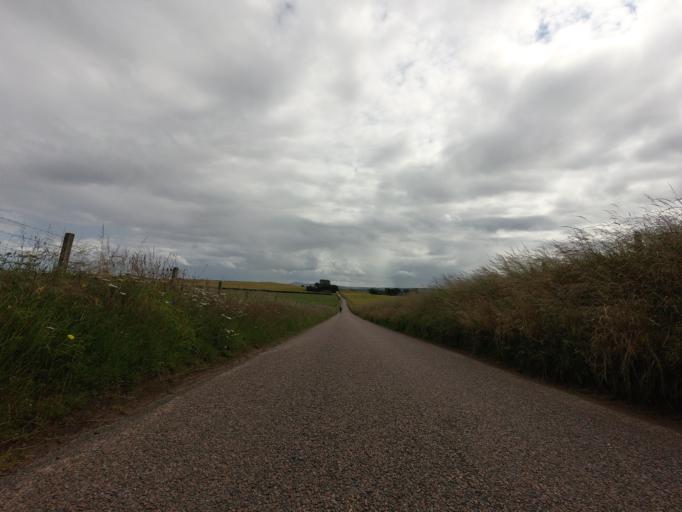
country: GB
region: Scotland
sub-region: Moray
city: Lhanbryd
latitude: 57.6677
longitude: -3.1571
